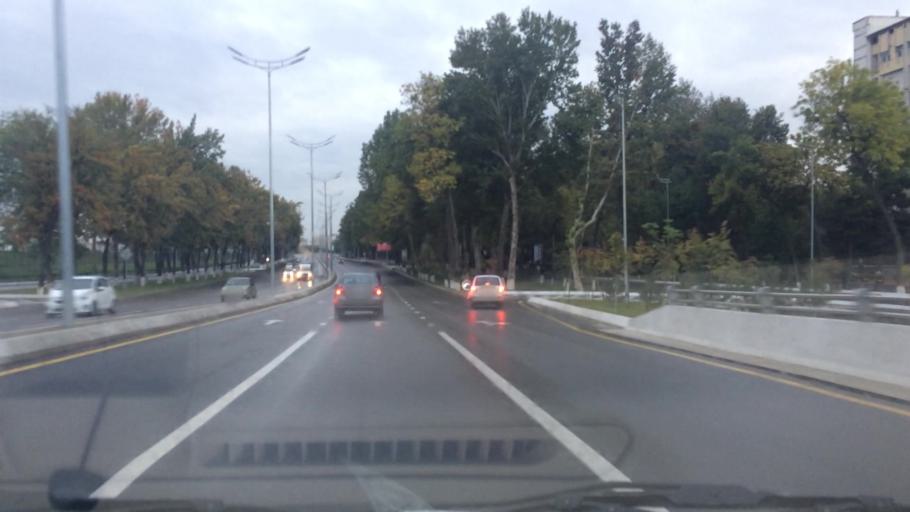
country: UZ
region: Toshkent Shahri
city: Tashkent
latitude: 41.2797
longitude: 69.2095
